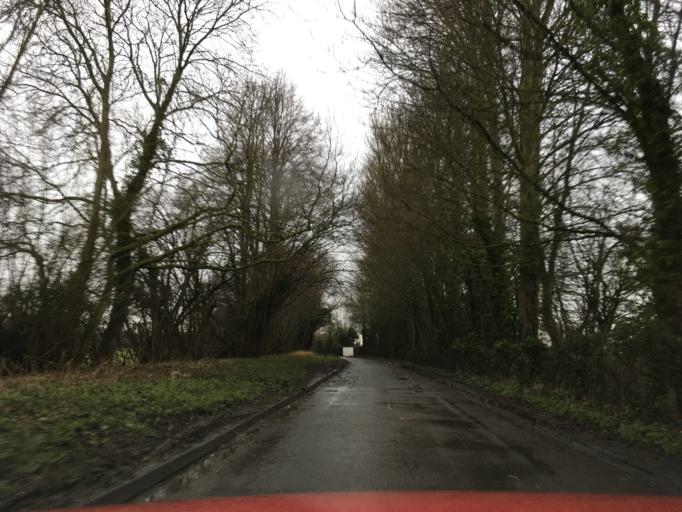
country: GB
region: England
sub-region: Oxfordshire
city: Oxford
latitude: 51.7614
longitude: -1.2864
